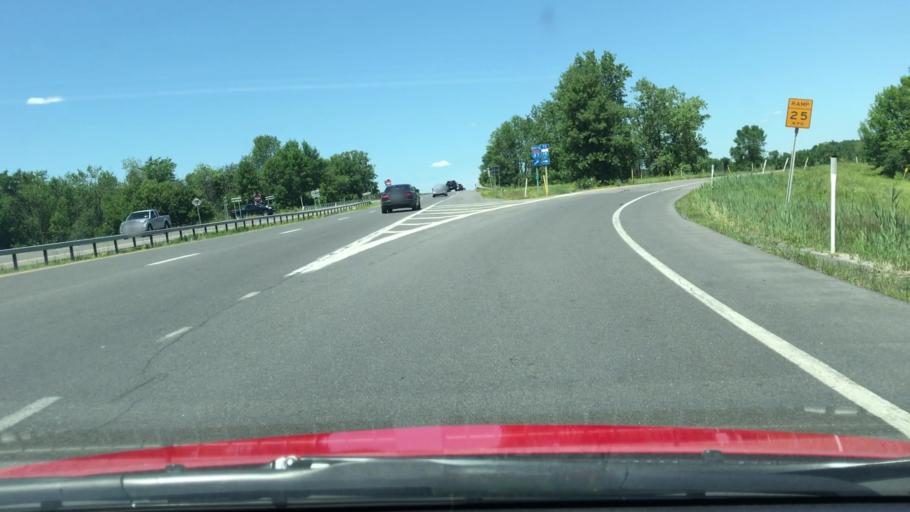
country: US
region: New York
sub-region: Clinton County
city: Plattsburgh
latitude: 44.7267
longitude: -73.4381
